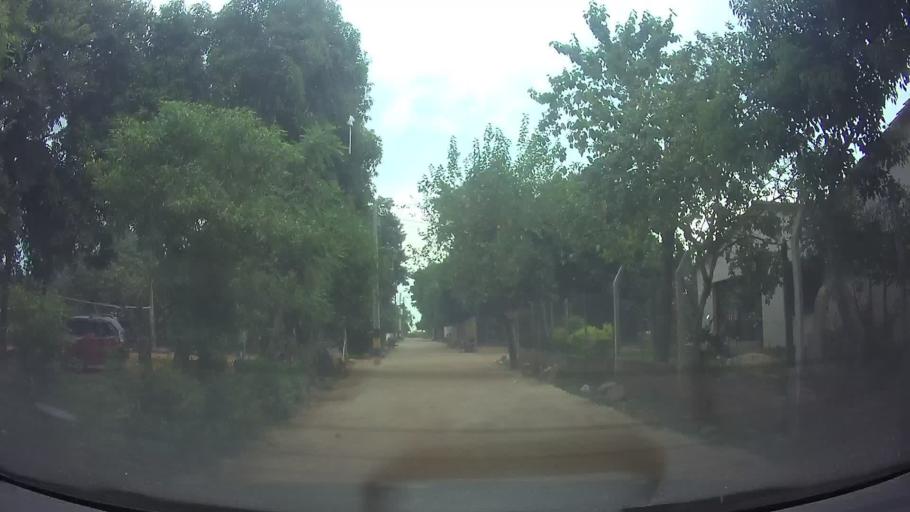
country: PY
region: Central
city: San Lorenzo
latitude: -25.2920
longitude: -57.4819
